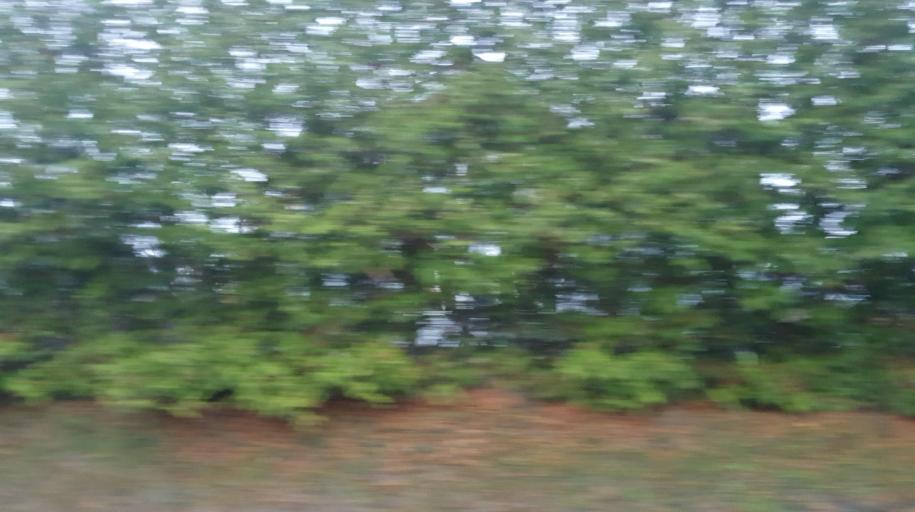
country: NO
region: Buskerud
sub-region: Modum
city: Vikersund
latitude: 59.8912
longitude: 9.9257
